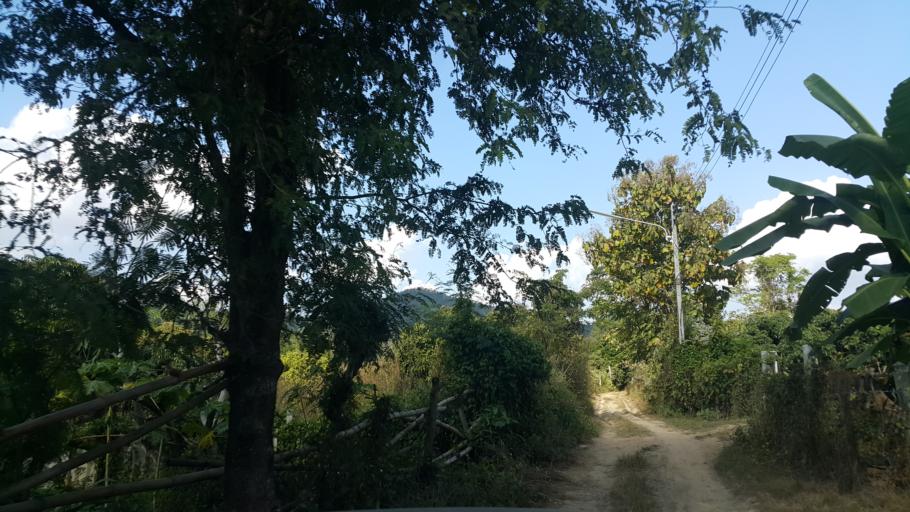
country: TH
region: Lamphun
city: Ban Thi
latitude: 18.5897
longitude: 99.1601
